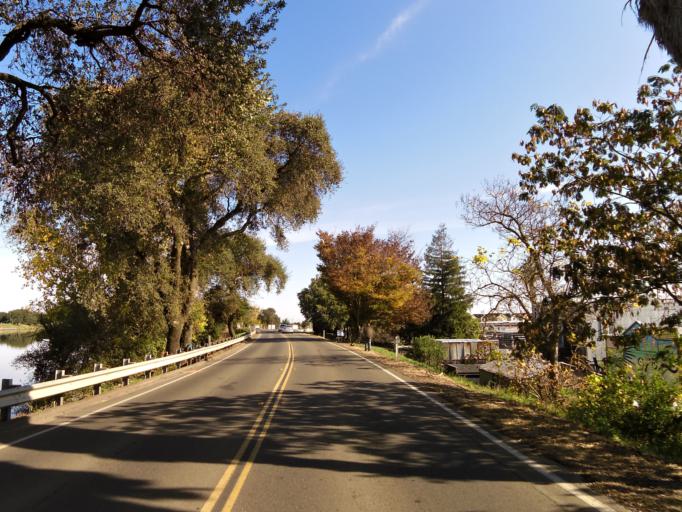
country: US
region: California
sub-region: Solano County
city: Rio Vista
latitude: 38.1631
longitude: -121.6056
